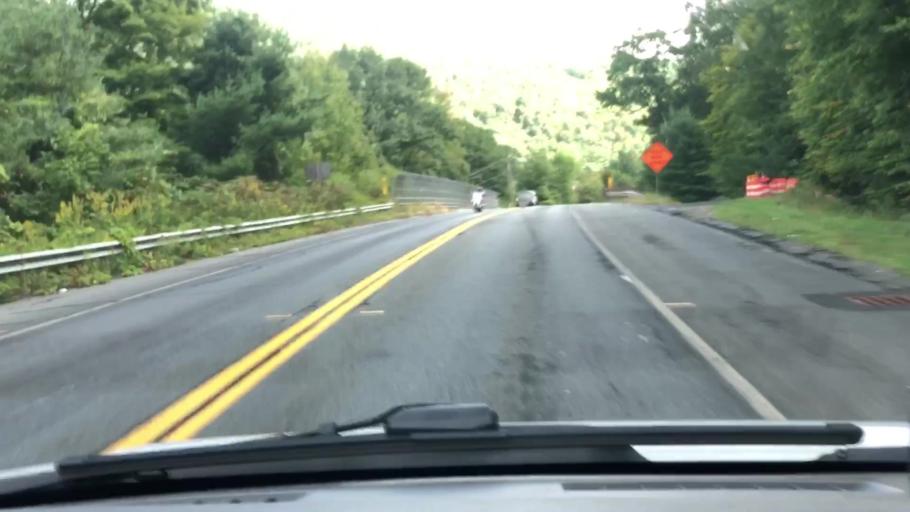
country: US
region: Massachusetts
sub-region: Franklin County
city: Charlemont
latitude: 42.6416
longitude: -72.9235
